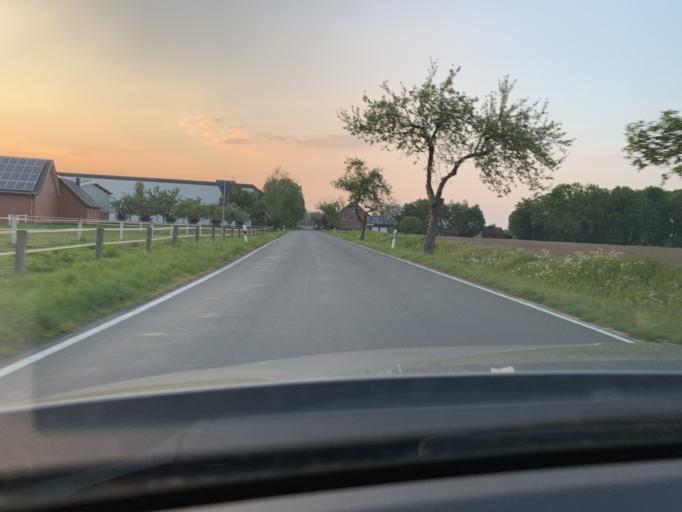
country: DE
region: North Rhine-Westphalia
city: Rietberg
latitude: 51.7732
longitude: 8.3805
